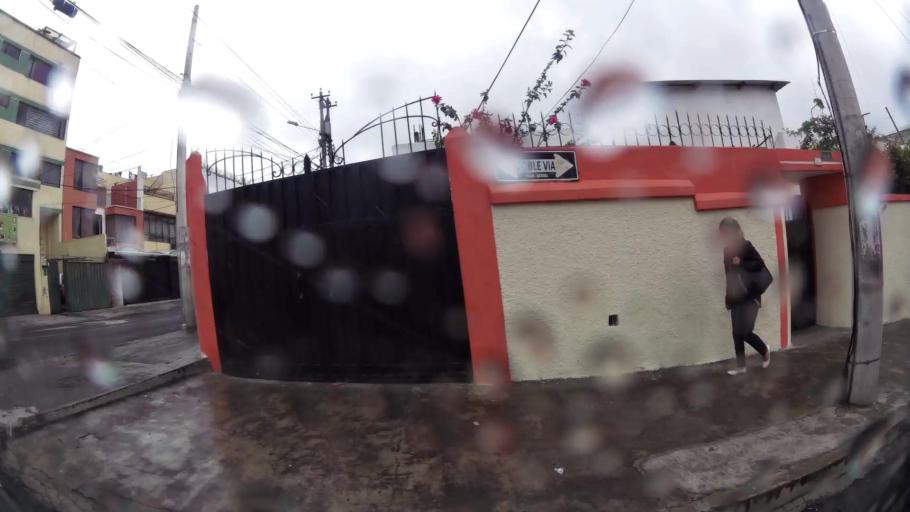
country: EC
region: Pichincha
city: Quito
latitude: -0.1237
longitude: -78.5009
